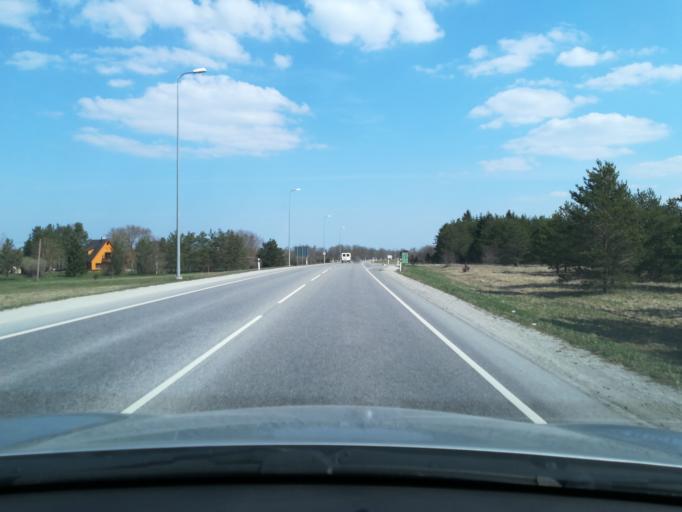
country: EE
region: Harju
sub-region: Saue linn
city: Saue
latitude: 59.3617
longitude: 24.4999
